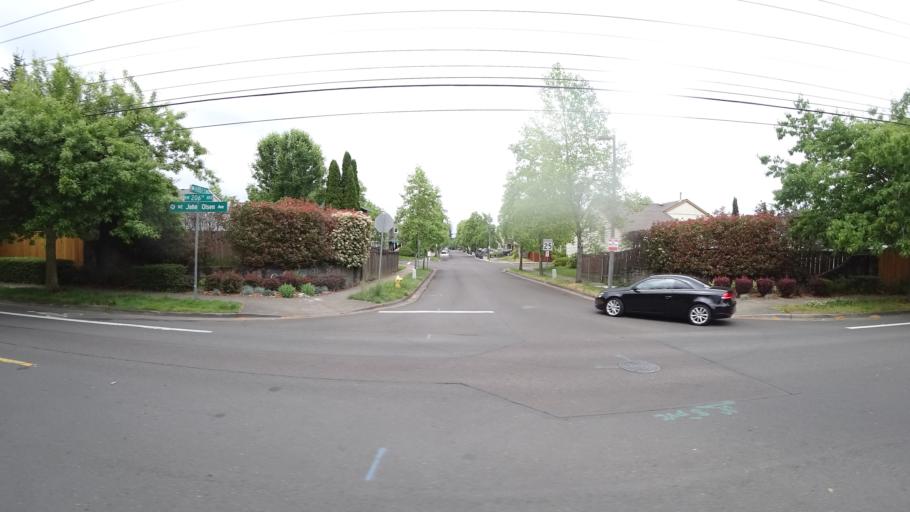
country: US
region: Oregon
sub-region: Washington County
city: Rockcreek
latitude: 45.5295
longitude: -122.8890
